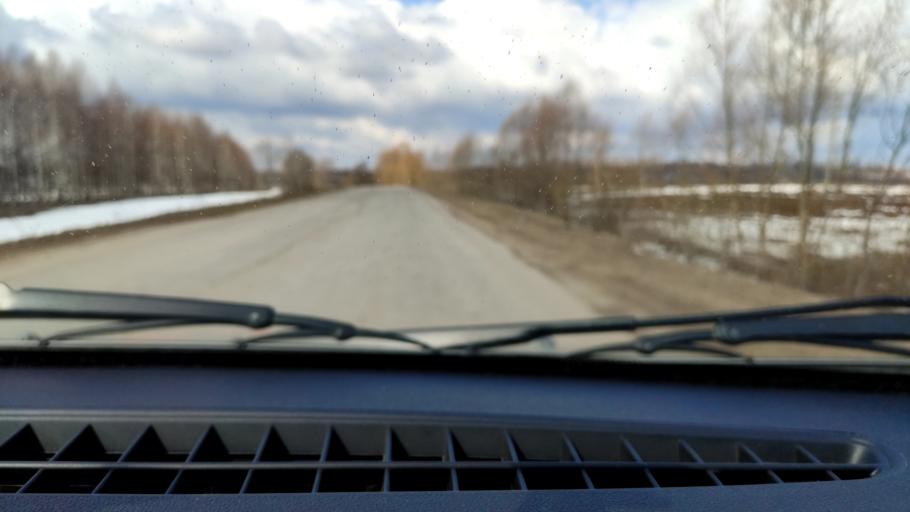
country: RU
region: Bashkortostan
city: Kudeyevskiy
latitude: 54.8601
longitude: 56.7762
